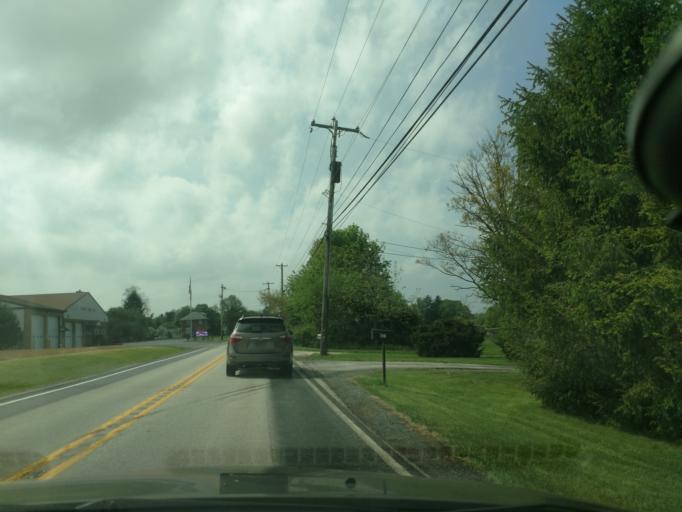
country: US
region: Pennsylvania
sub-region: Chester County
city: Kenilworth
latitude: 40.1739
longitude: -75.6155
